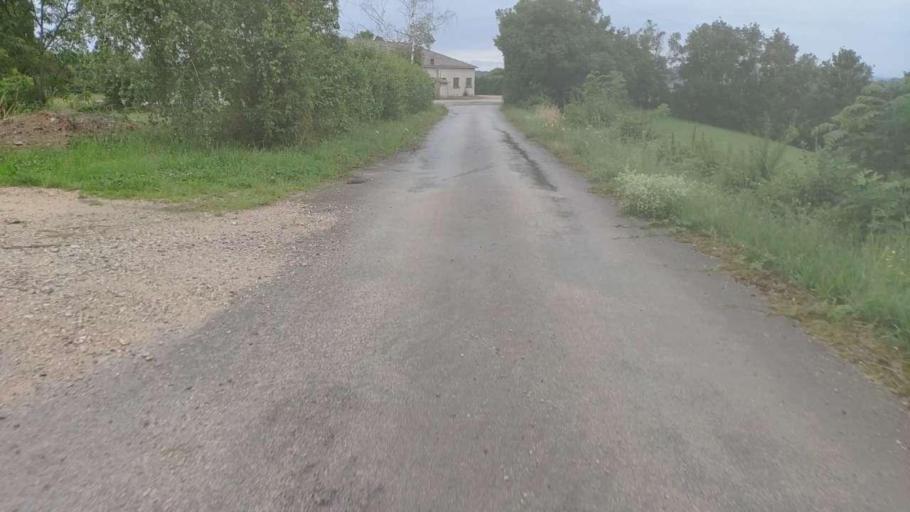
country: FR
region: Franche-Comte
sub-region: Departement du Jura
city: Poligny
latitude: 46.7904
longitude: 5.6153
